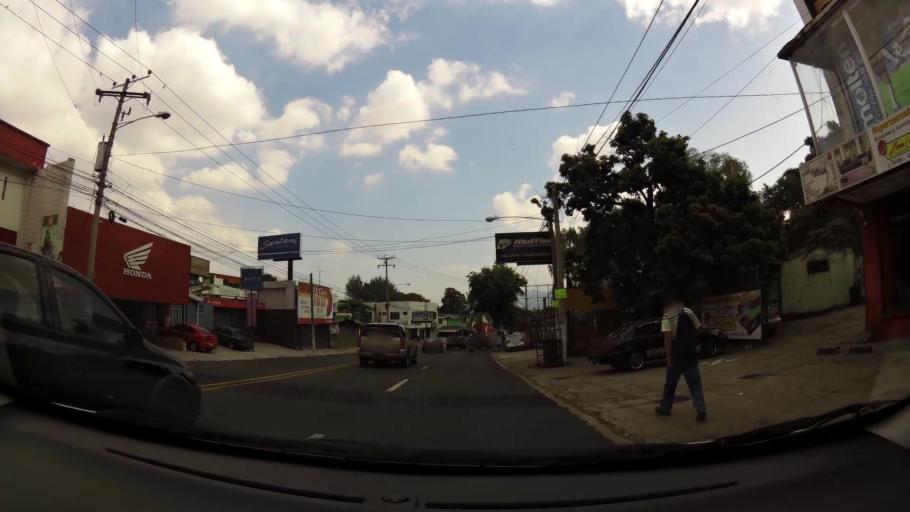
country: SV
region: San Salvador
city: Mejicanos
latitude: 13.7050
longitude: -89.2226
